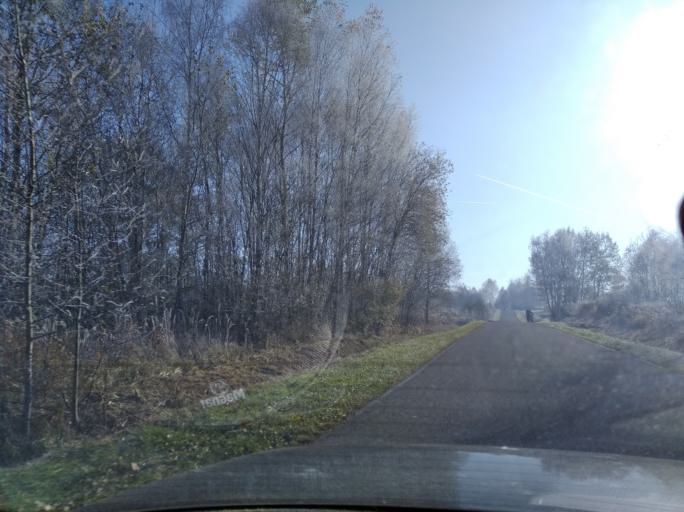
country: PL
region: Subcarpathian Voivodeship
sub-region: Powiat strzyzowski
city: Wysoka Strzyzowska
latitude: 49.8407
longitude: 21.7085
